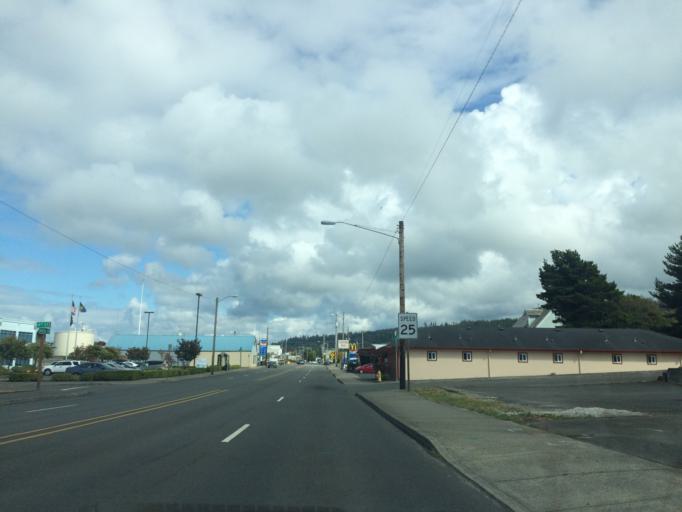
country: US
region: Oregon
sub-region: Clatsop County
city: Astoria
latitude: 46.1905
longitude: -123.8392
